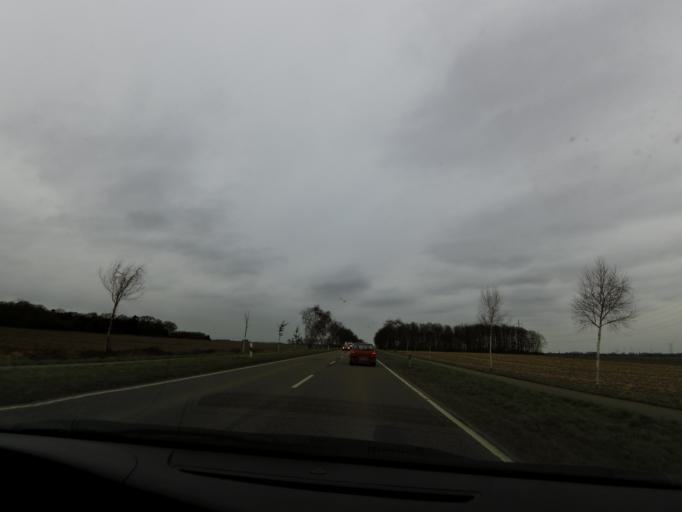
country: DE
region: North Rhine-Westphalia
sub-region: Regierungsbezirk Koln
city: Selfkant
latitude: 51.0049
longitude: 5.9507
